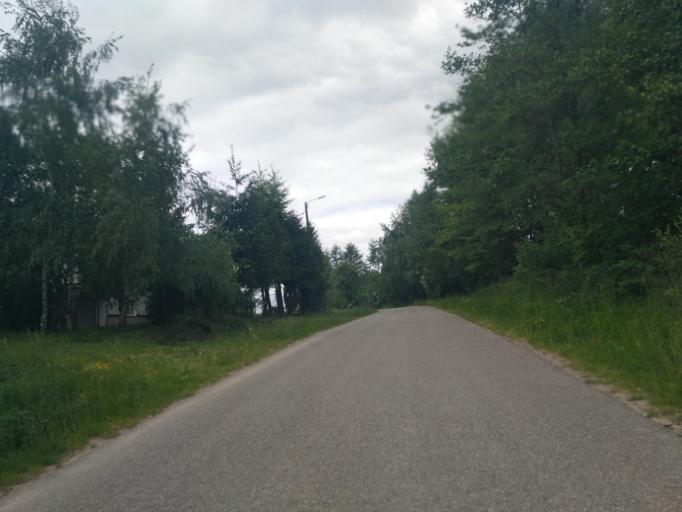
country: PL
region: Subcarpathian Voivodeship
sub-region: Powiat jasielski
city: Tarnowiec
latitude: 49.6945
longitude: 21.5811
